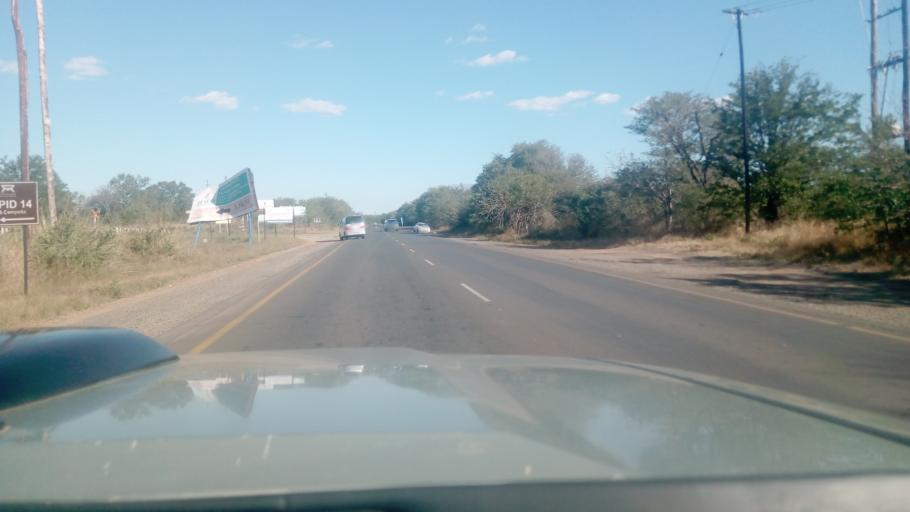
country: ZW
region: Matabeleland North
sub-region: Hwange District
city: Victoria Falls
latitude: -17.9191
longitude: 25.8668
